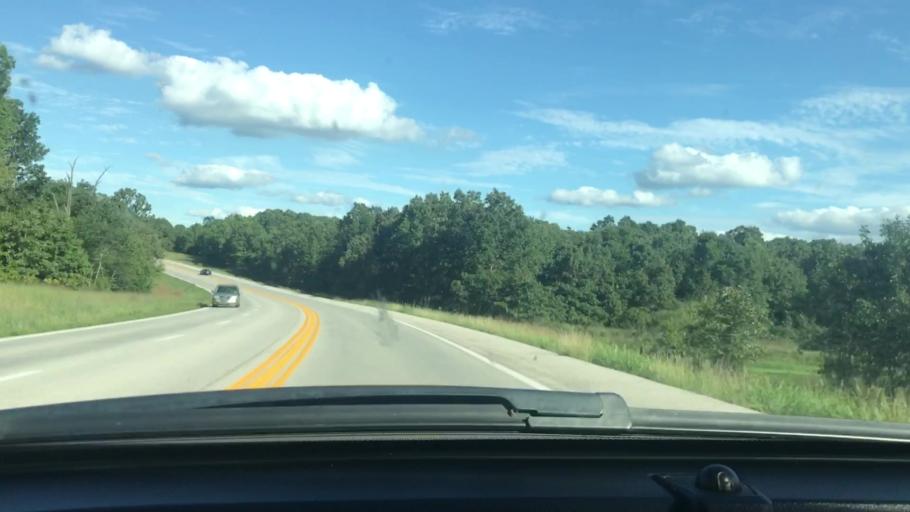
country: US
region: Missouri
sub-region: Howell County
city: West Plains
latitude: 36.6609
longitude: -91.7195
